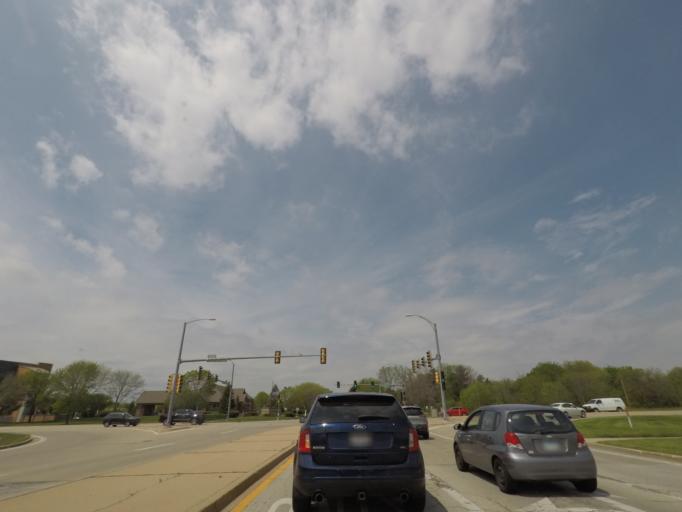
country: US
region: Illinois
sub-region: Winnebago County
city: Machesney Park
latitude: 42.3043
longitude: -88.9787
